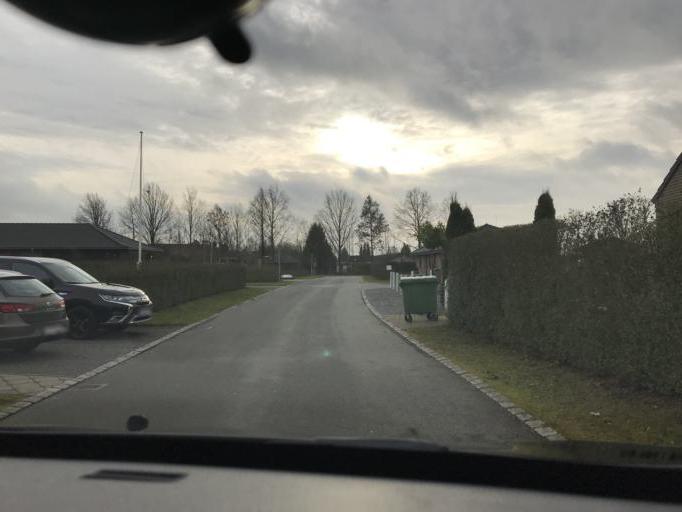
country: DK
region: South Denmark
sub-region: Faaborg-Midtfyn Kommune
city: Ringe
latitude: 55.2477
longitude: 10.4692
